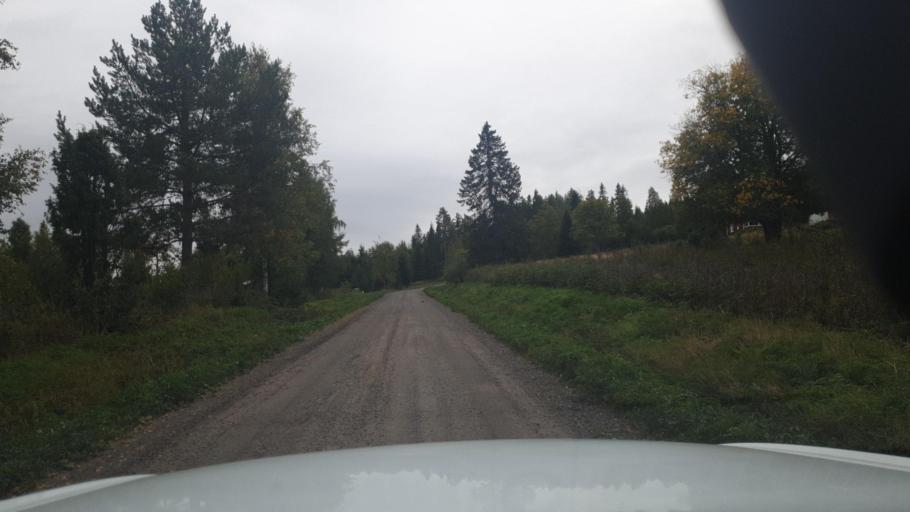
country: SE
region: Vaermland
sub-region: Torsby Kommun
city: Torsby
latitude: 60.1830
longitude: 12.6449
